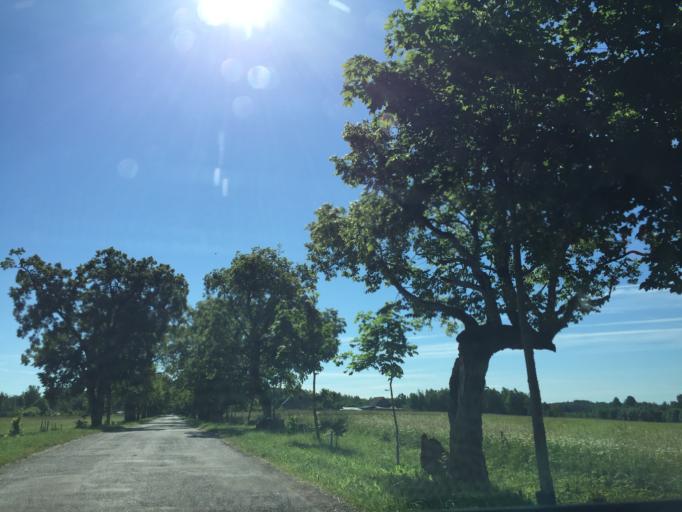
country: LV
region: Kuldigas Rajons
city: Kuldiga
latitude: 57.3258
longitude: 22.0237
